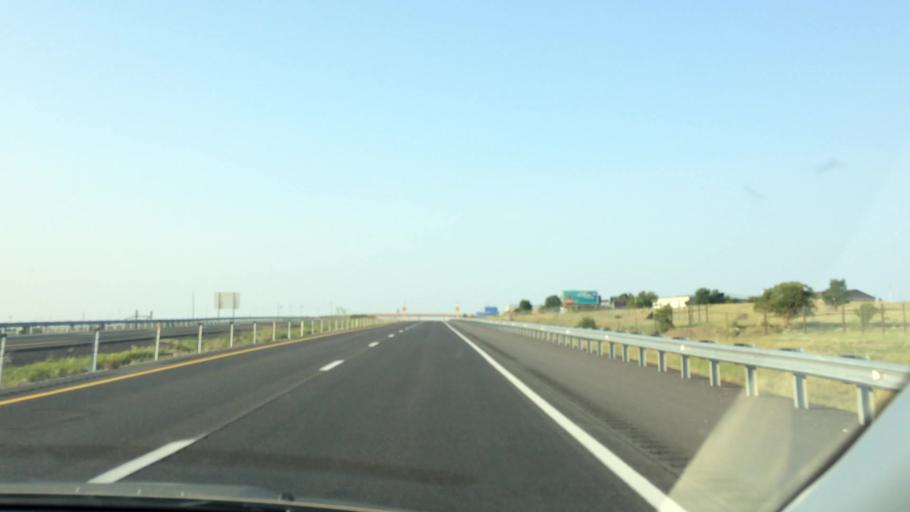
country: US
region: New Mexico
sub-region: Colfax County
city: Raton
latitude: 36.8755
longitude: -104.4351
